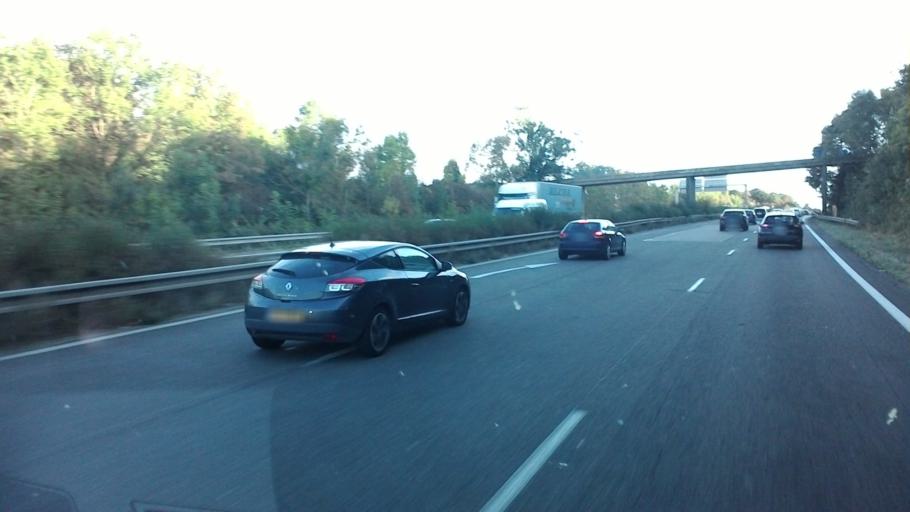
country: FR
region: Lorraine
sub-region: Departement de la Moselle
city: Illange
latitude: 49.3408
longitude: 6.1819
